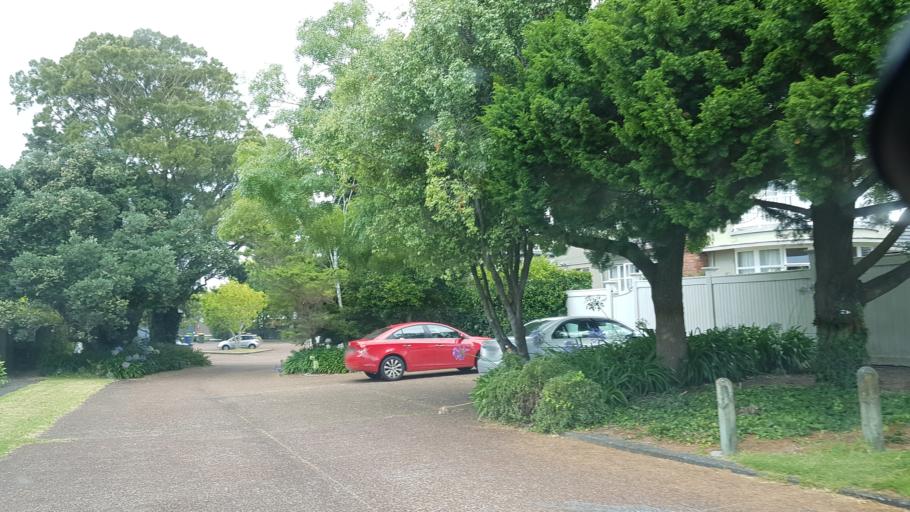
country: NZ
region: Auckland
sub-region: Auckland
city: North Shore
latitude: -36.8031
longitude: 174.7845
